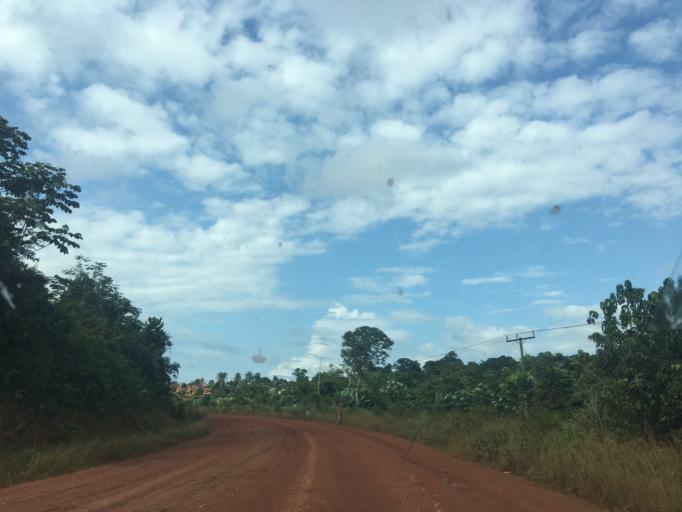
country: GH
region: Western
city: Wassa-Akropong
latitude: 5.9551
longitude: -2.4338
